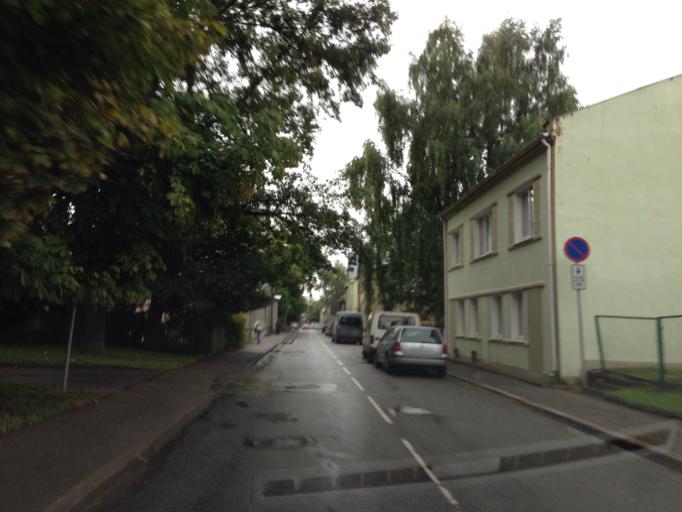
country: EE
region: Tartu
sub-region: Tartu linn
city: Tartu
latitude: 58.3742
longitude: 26.7123
